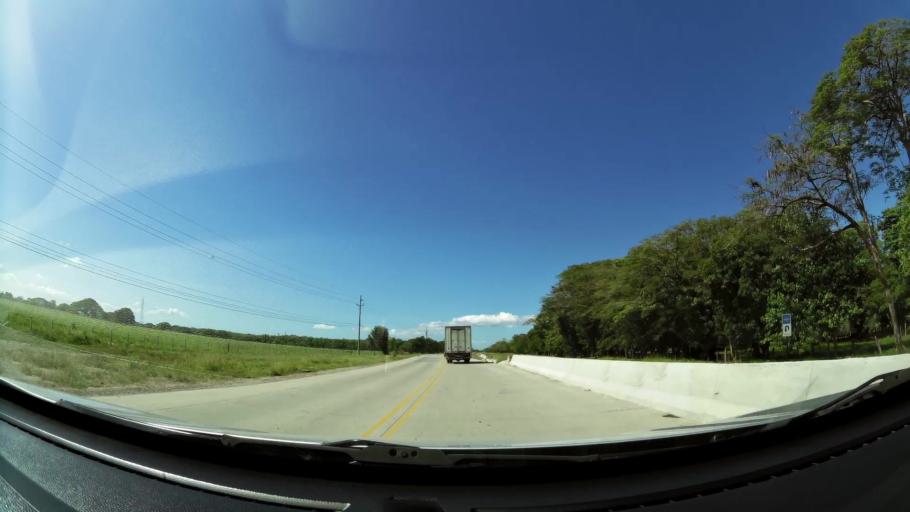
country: CR
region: Guanacaste
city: Liberia
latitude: 10.5724
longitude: -85.3966
